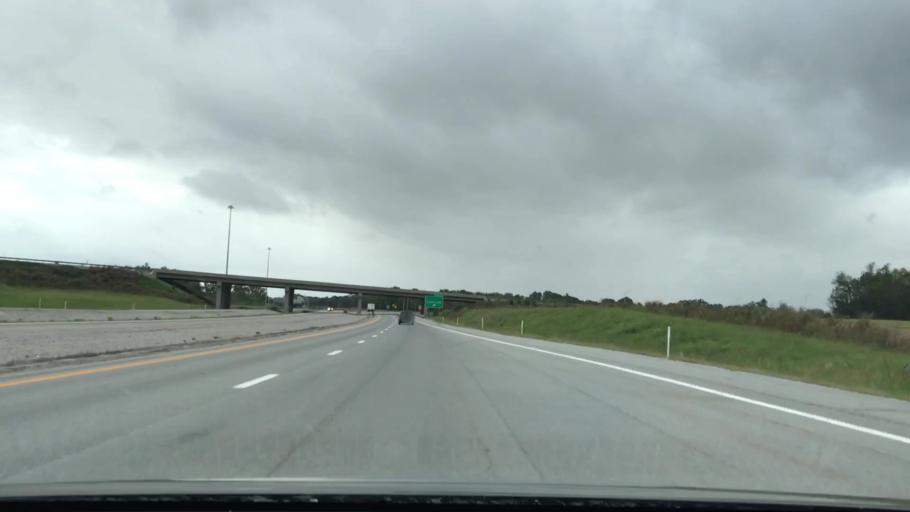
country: US
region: Kentucky
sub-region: Christian County
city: Hopkinsville
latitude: 36.8127
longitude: -87.4871
